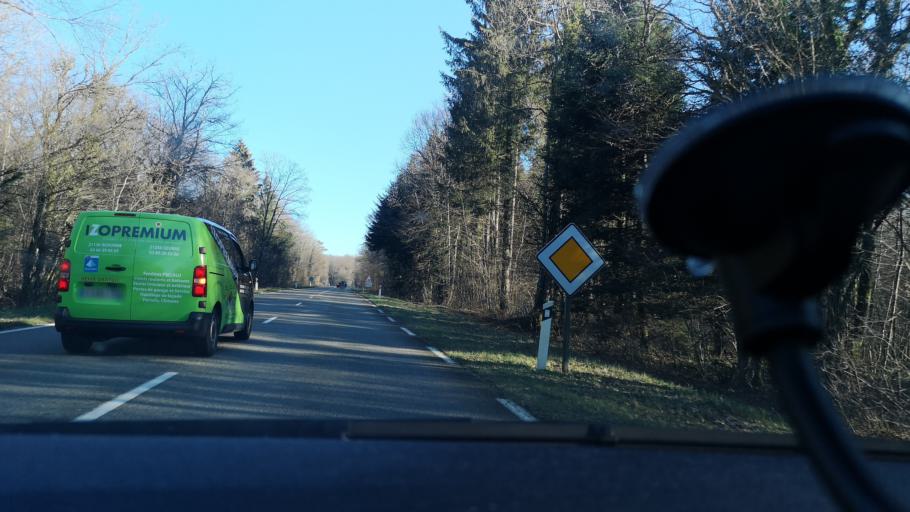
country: FR
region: Franche-Comte
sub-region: Departement du Jura
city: Poligny
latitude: 46.8161
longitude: 5.7612
